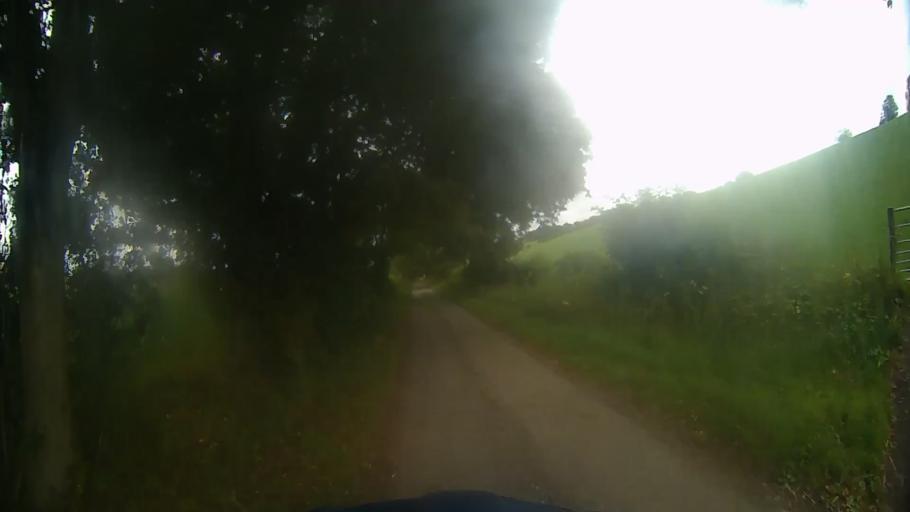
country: GB
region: England
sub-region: Hampshire
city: Overton
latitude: 51.2656
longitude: -1.3197
